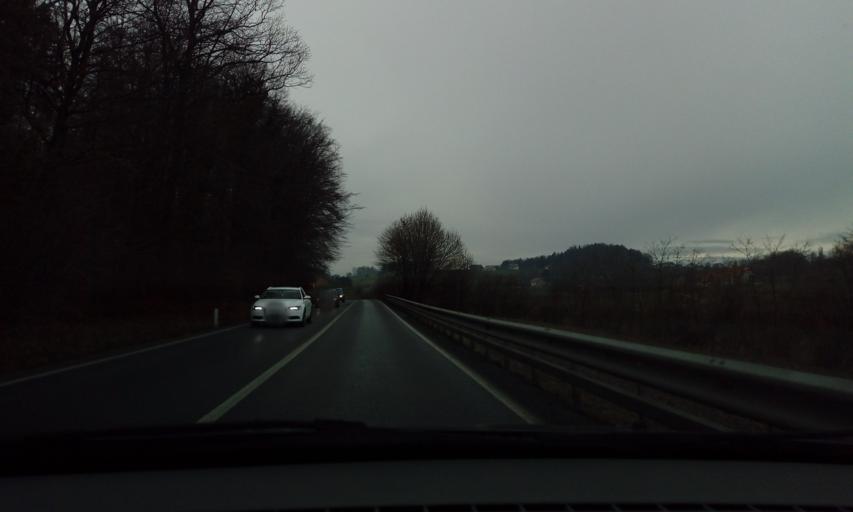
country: SI
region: Smarje pri Jelsah
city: Smarje pri Jelsah
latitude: 46.2302
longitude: 15.4979
